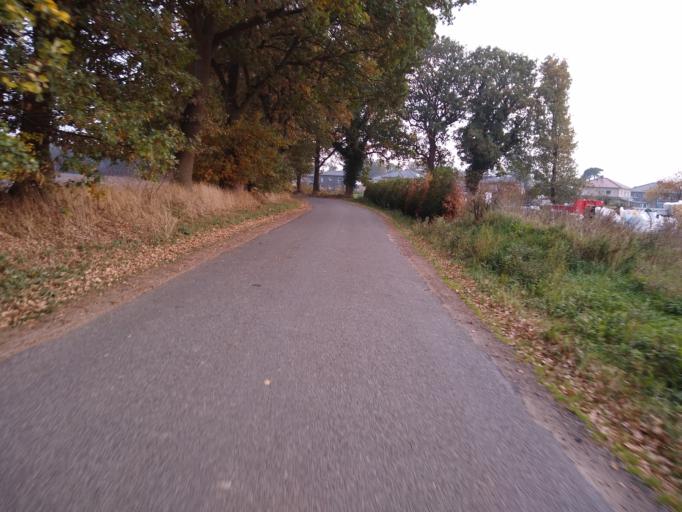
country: DE
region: Lower Saxony
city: Rastede
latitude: 53.2123
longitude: 8.2339
